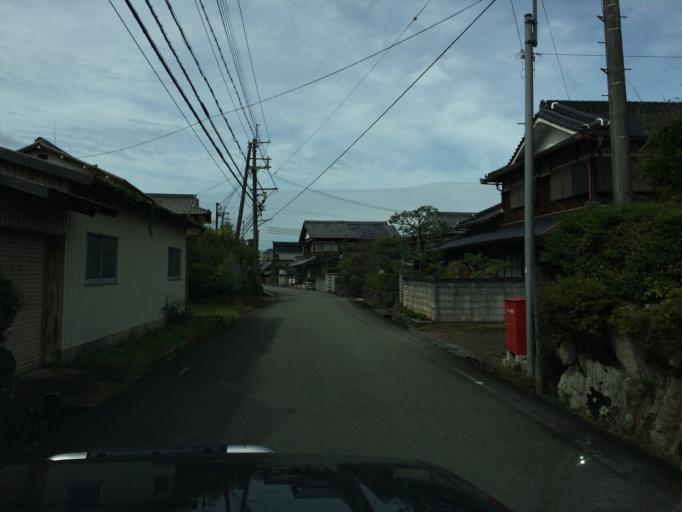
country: JP
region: Hyogo
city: Sasayama
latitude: 35.0723
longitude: 135.3642
